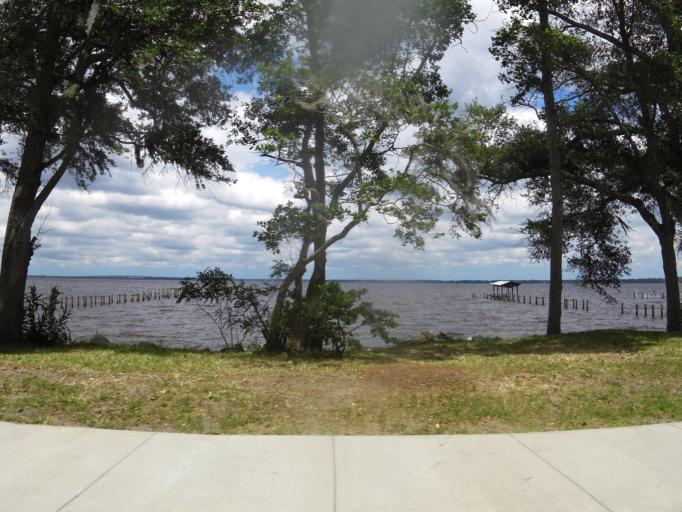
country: US
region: Florida
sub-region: Clay County
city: Orange Park
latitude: 30.1726
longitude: -81.6969
